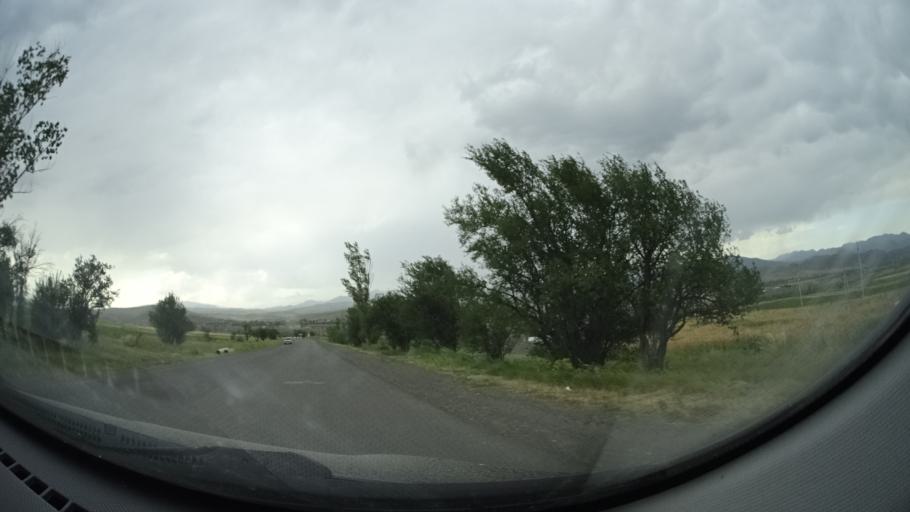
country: GE
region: Samtskhe-Javakheti
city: Akhaltsikhe
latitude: 41.6408
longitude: 43.0283
